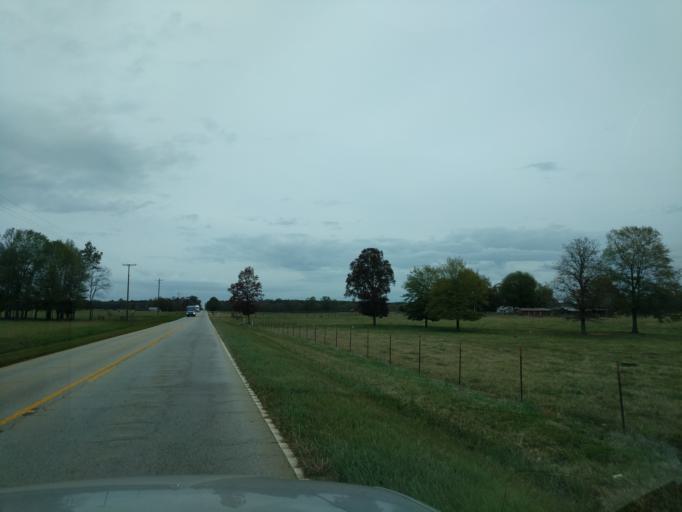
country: US
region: South Carolina
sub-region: Saluda County
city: Saluda
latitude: 34.1059
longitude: -81.7498
